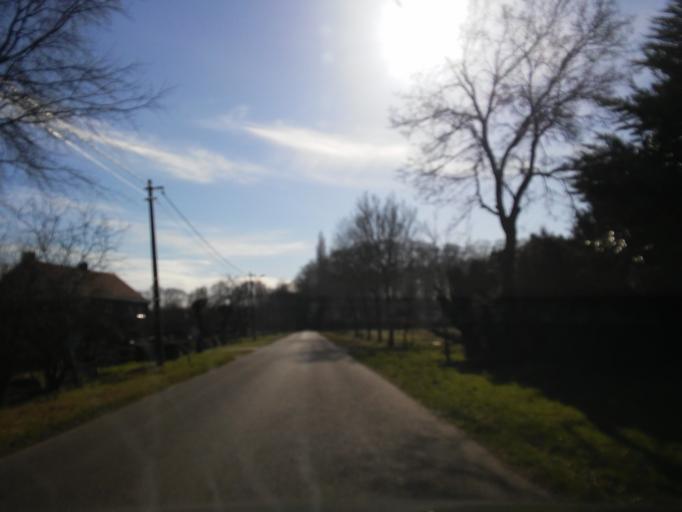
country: BE
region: Flanders
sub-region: Provincie Oost-Vlaanderen
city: Maldegem
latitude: 51.1570
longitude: 3.4755
